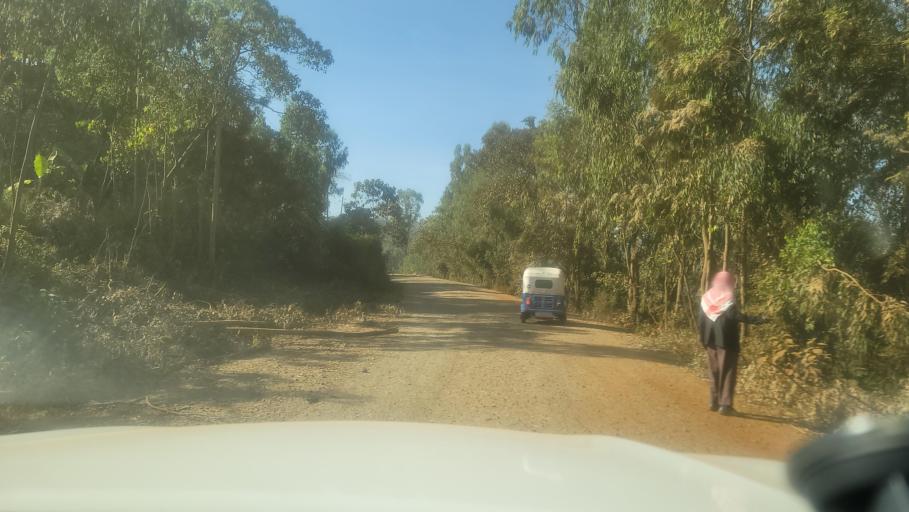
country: ET
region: Oromiya
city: Agaro
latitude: 7.8376
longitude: 36.5422
